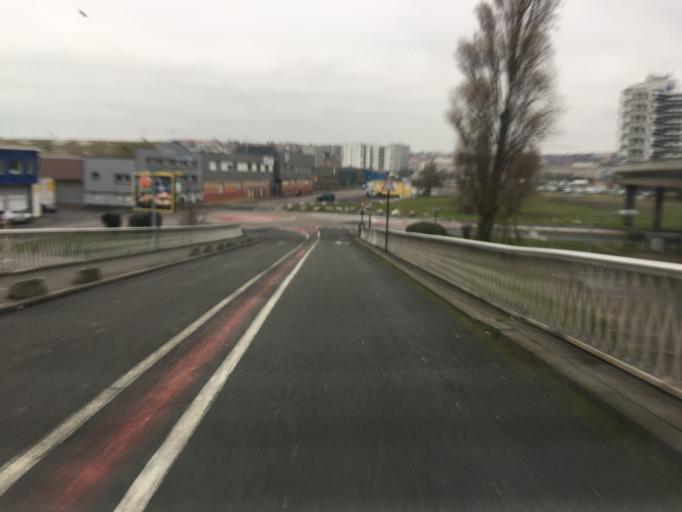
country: FR
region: Nord-Pas-de-Calais
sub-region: Departement du Pas-de-Calais
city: Outreau
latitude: 50.7185
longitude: 1.5969
